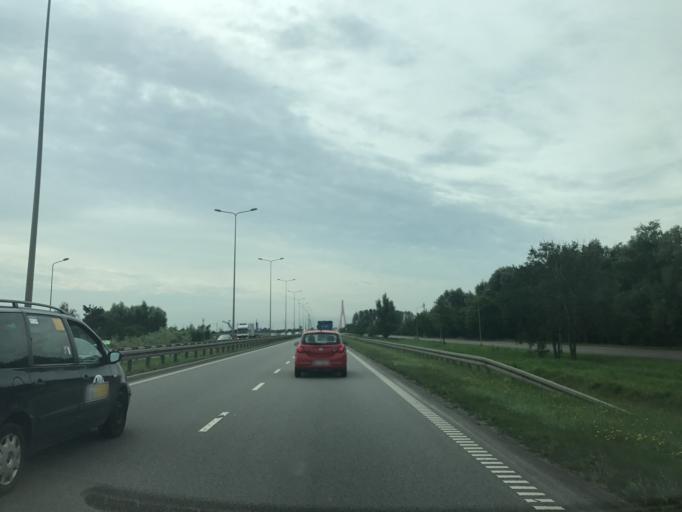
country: PL
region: Pomeranian Voivodeship
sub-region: Gdansk
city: Gdansk
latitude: 54.3703
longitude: 18.6852
